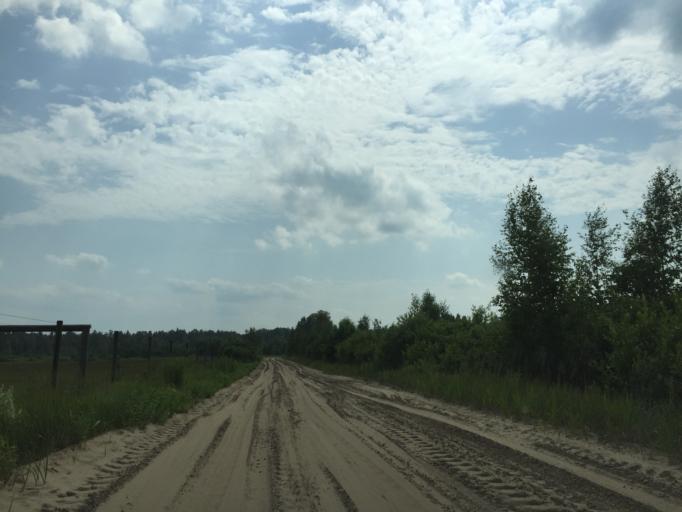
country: LV
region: Ozolnieku
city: Ozolnieki
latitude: 56.7606
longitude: 23.7533
